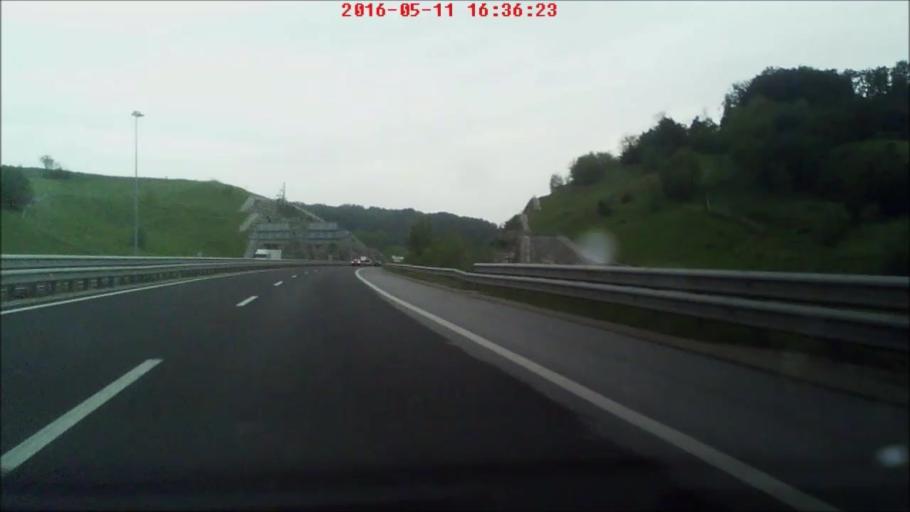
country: SI
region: Pesnica
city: Pesnica pri Mariboru
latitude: 46.5866
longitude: 15.6874
